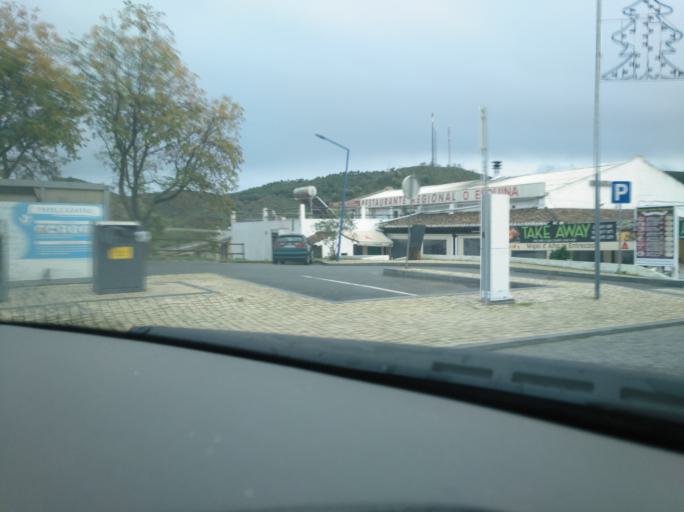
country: PT
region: Beja
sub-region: Mertola
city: Mertola
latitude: 37.6416
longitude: -7.6589
